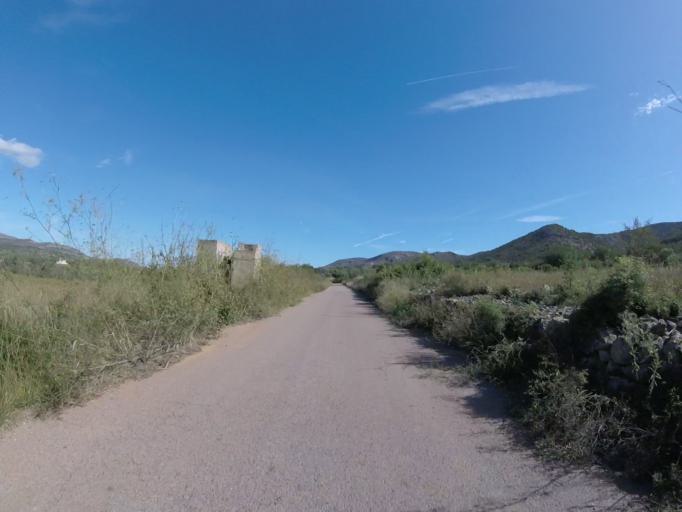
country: ES
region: Valencia
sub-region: Provincia de Castello
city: Santa Magdalena de Pulpis
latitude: 40.3596
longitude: 0.3117
